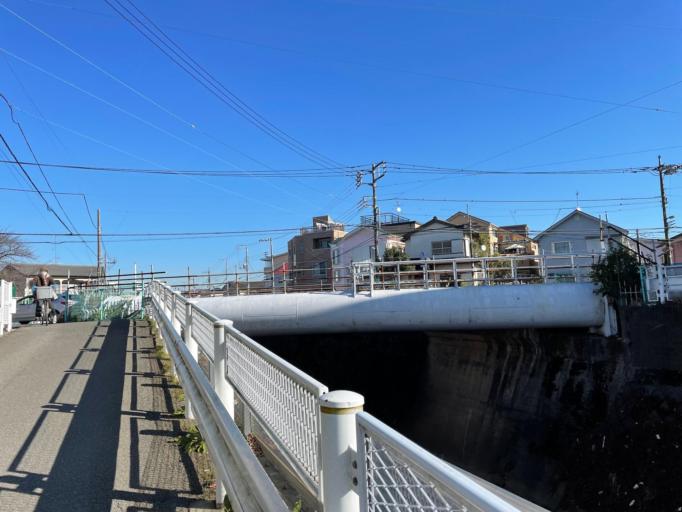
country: JP
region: Tokyo
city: Chofugaoka
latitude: 35.6330
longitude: 139.5436
